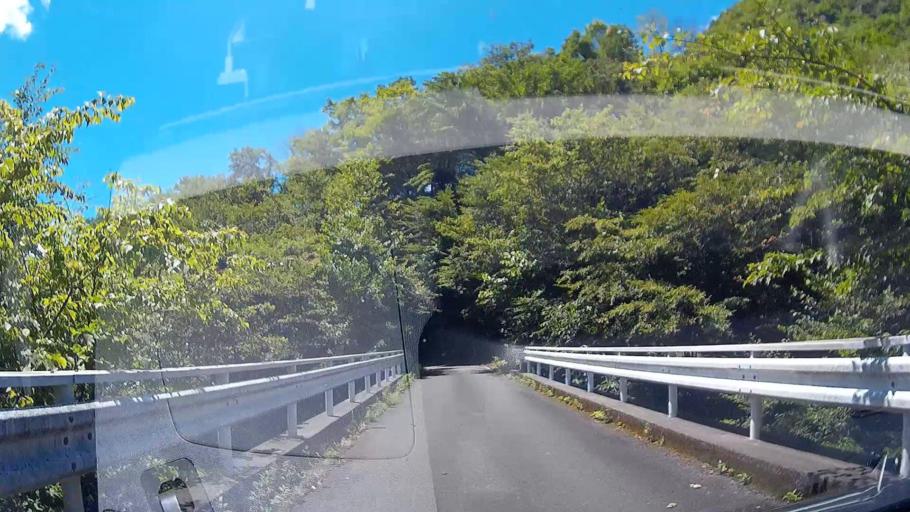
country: JP
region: Shizuoka
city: Fujinomiya
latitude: 35.2917
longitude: 138.3189
